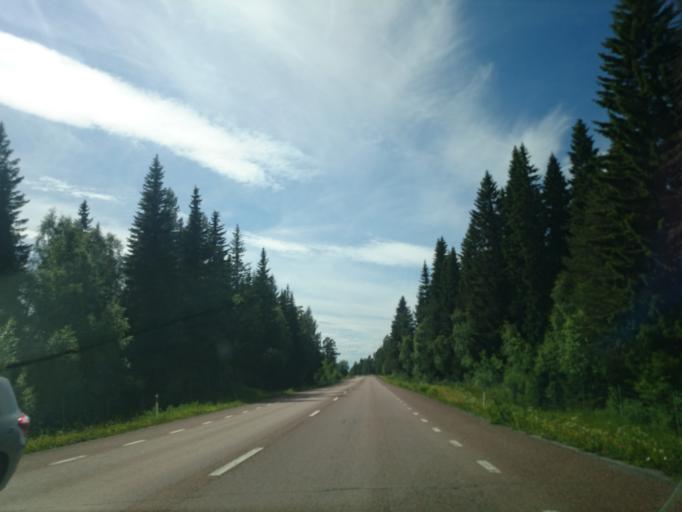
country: SE
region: Jaemtland
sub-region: Krokoms Kommun
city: Krokom
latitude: 63.3257
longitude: 14.3152
